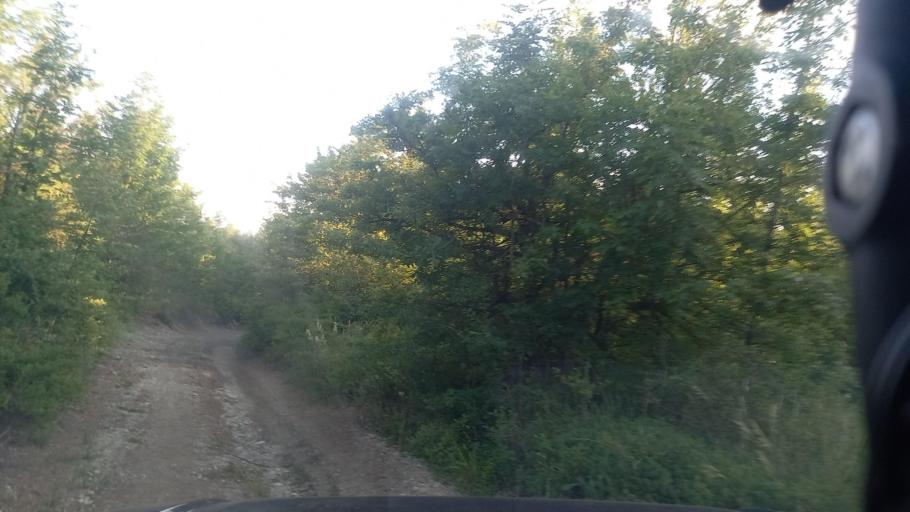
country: RU
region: Krasnodarskiy
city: Pshada
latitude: 44.5936
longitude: 38.2814
